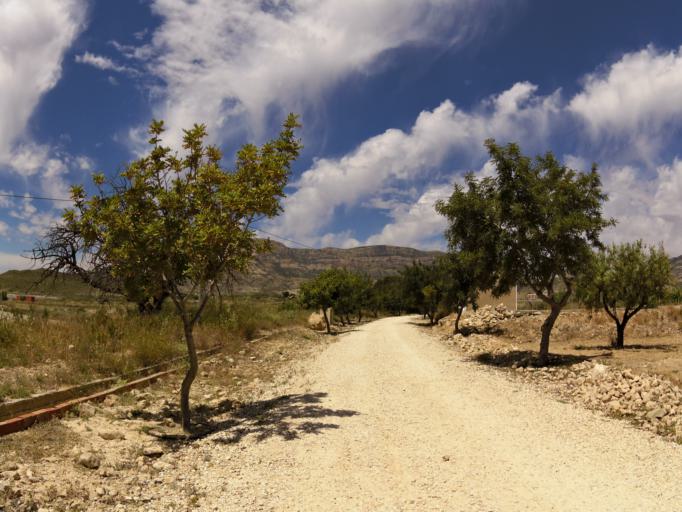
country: ES
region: Valencia
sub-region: Provincia de Alicante
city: Agost
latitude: 38.4449
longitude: -0.6652
